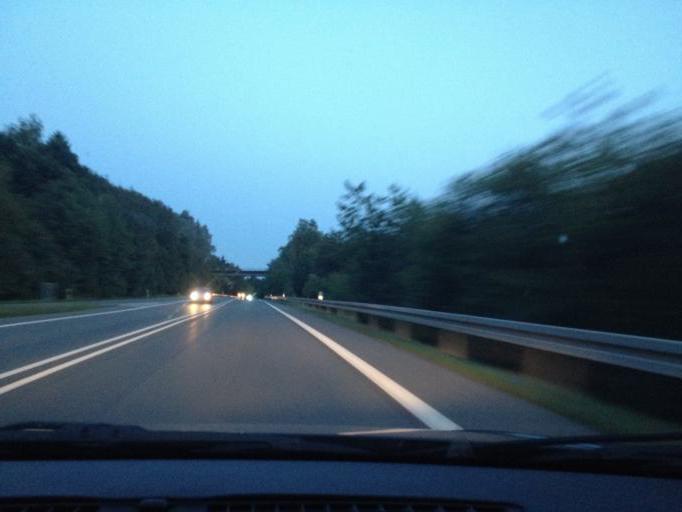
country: DE
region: Saarland
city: Namborn
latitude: 49.5024
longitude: 7.1476
